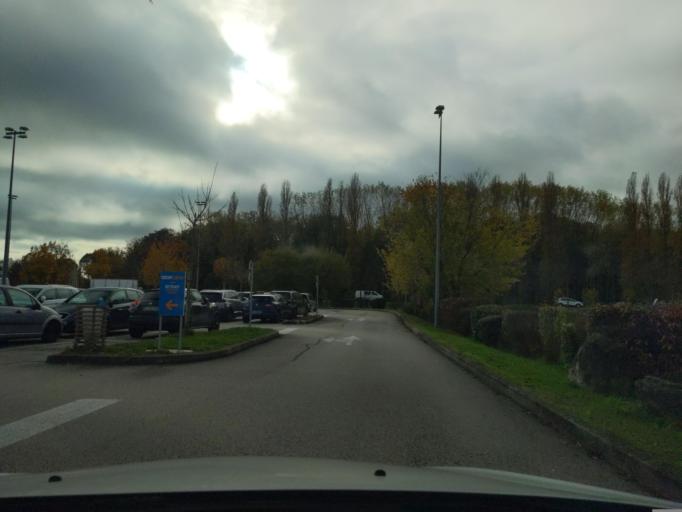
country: FR
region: Bourgogne
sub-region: Departement de la Cote-d'Or
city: Saint-Apollinaire
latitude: 47.3152
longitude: 5.0879
